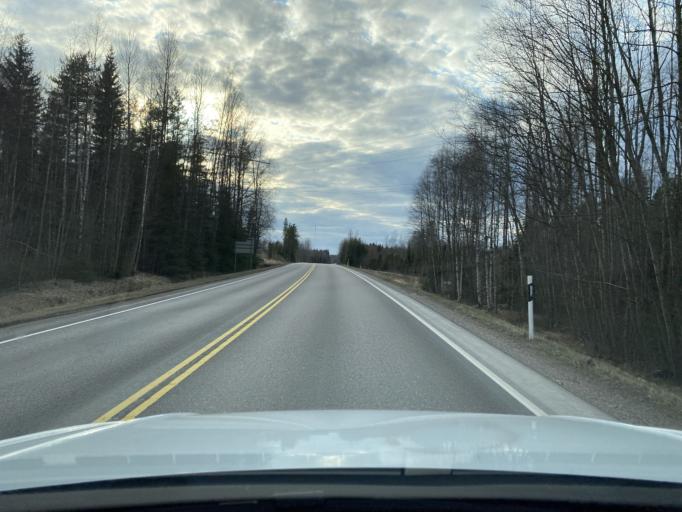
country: FI
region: Haeme
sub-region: Haemeenlinna
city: Renko
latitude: 60.7827
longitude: 24.1575
